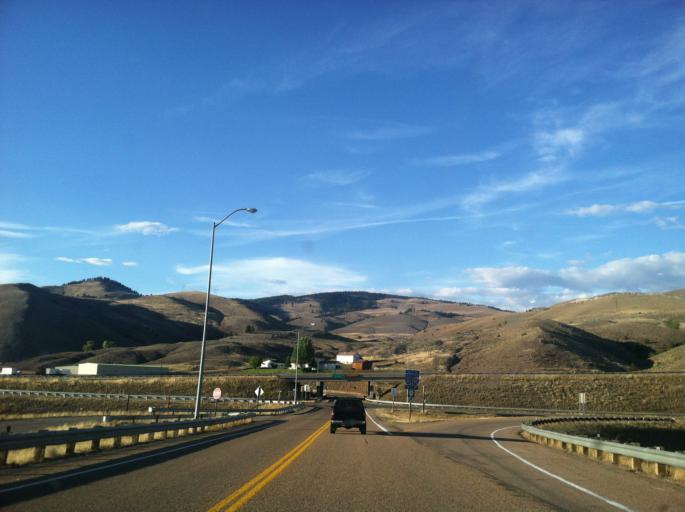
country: US
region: Montana
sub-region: Granite County
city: Philipsburg
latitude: 46.6704
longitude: -113.1538
